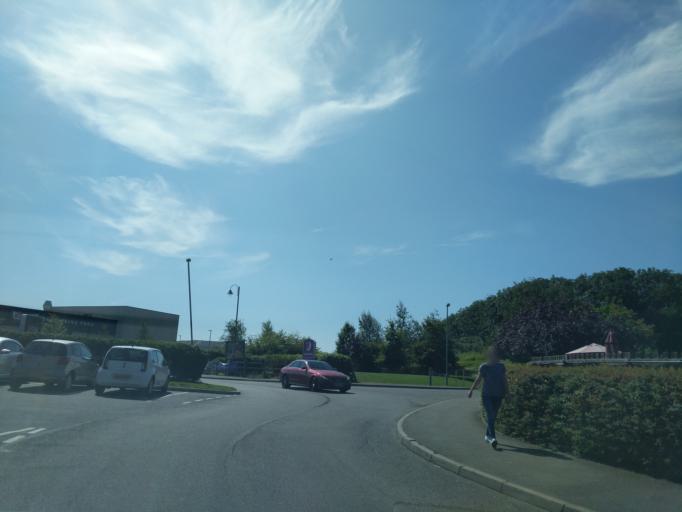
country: GB
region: England
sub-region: Cambridgeshire
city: Yaxley
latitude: 52.5401
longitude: -0.2570
